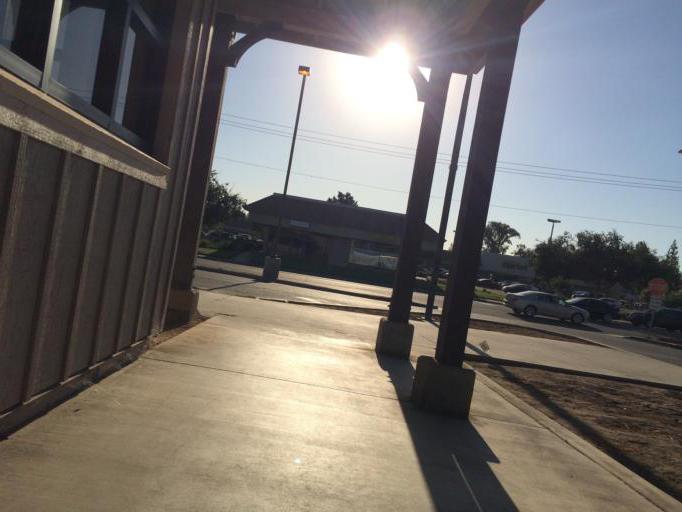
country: US
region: California
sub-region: Fresno County
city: Clovis
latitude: 36.8219
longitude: -119.7086
